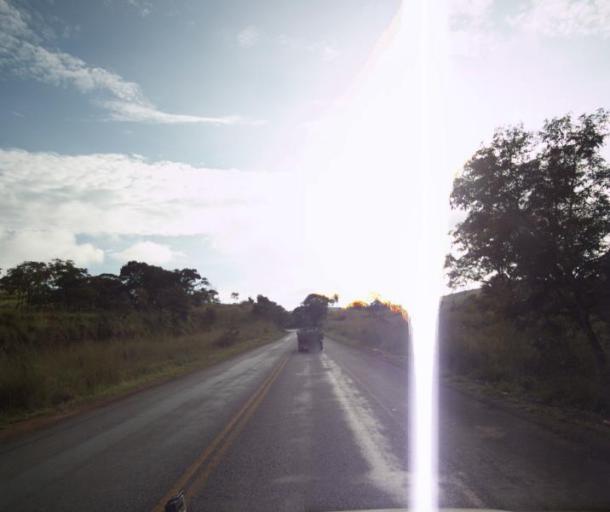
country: BR
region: Goias
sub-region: Pirenopolis
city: Pirenopolis
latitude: -15.7100
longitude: -48.6922
